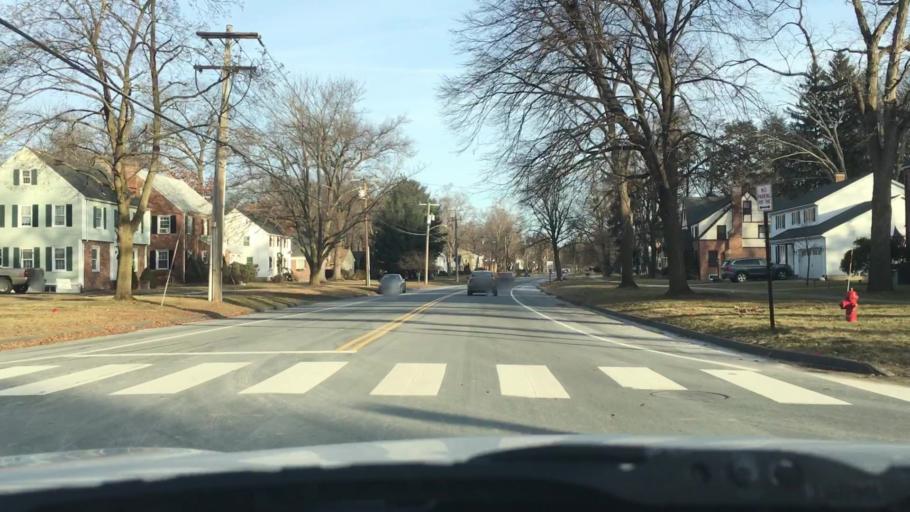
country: US
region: Massachusetts
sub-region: Hampden County
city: Longmeadow
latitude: 42.0499
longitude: -72.5733
